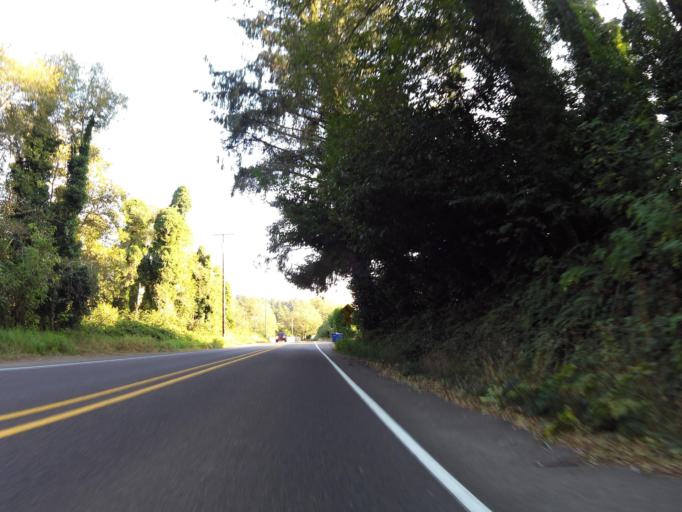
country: US
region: Oregon
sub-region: Lincoln County
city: Lincoln City
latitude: 45.0029
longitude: -123.9794
